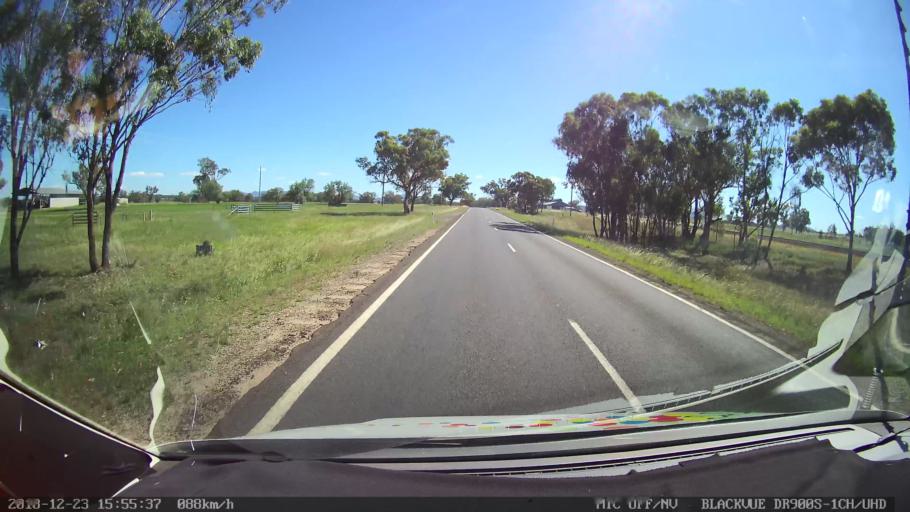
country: AU
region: New South Wales
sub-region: Tamworth Municipality
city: Phillip
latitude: -31.1573
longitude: 150.8666
